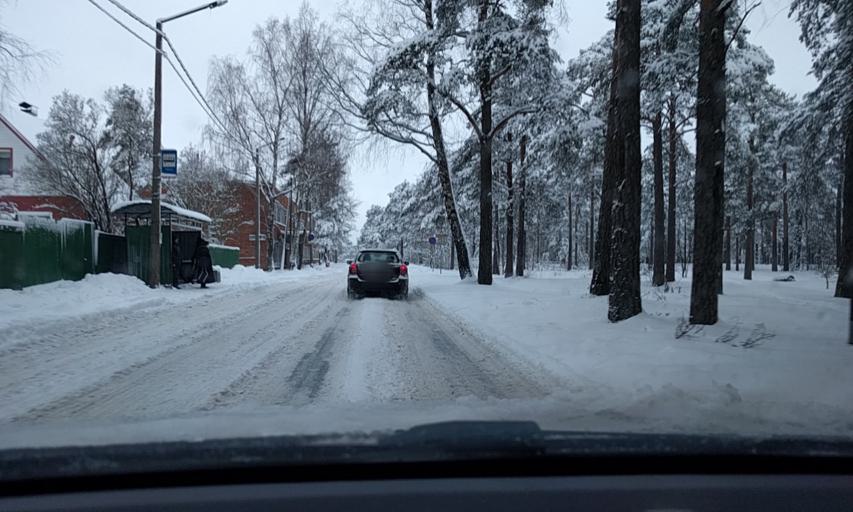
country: EE
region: Harju
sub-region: Saue vald
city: Laagri
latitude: 59.3928
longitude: 24.6631
